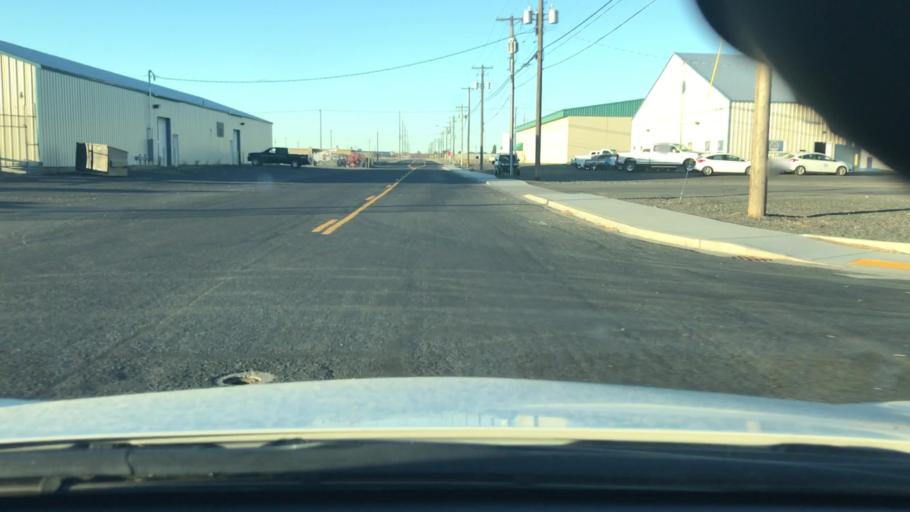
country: US
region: Washington
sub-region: Grant County
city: Moses Lake North
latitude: 47.1841
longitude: -119.3166
